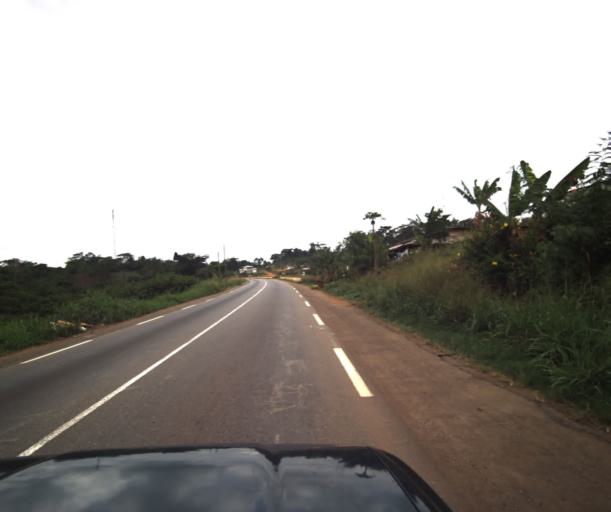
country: CM
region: Centre
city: Eseka
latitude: 3.8518
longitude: 10.9690
